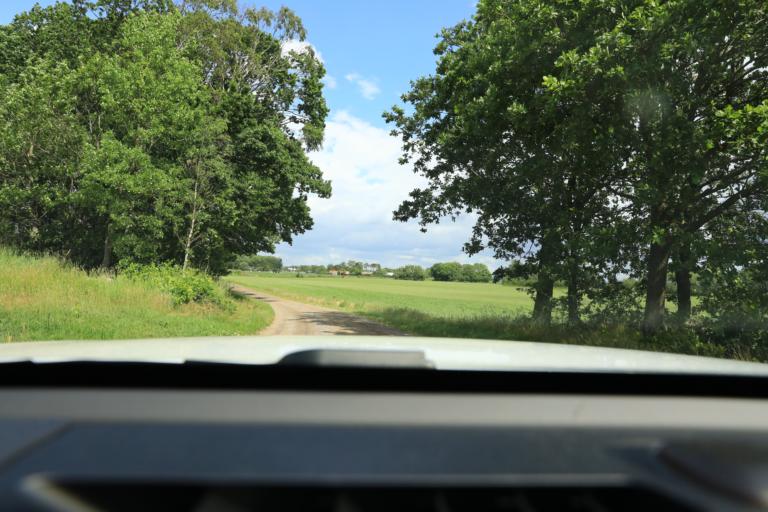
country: SE
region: Halland
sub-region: Varbergs Kommun
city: Tvaaker
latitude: 57.1084
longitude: 12.4042
